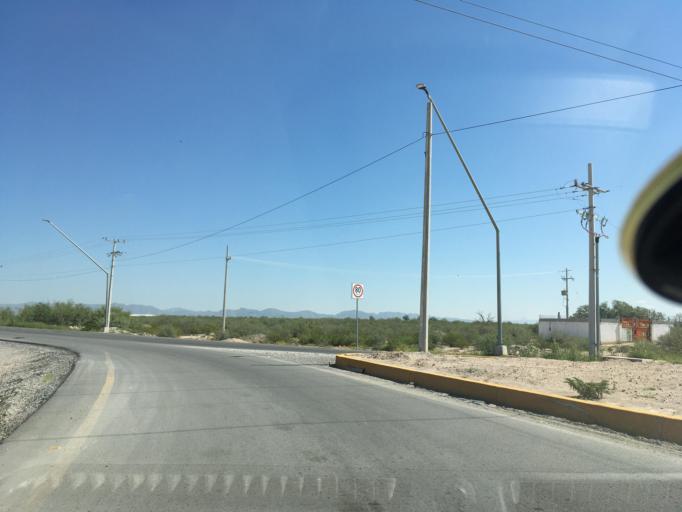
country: MX
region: Coahuila
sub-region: Torreon
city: Fraccionamiento la Noria
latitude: 25.4619
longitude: -103.3237
